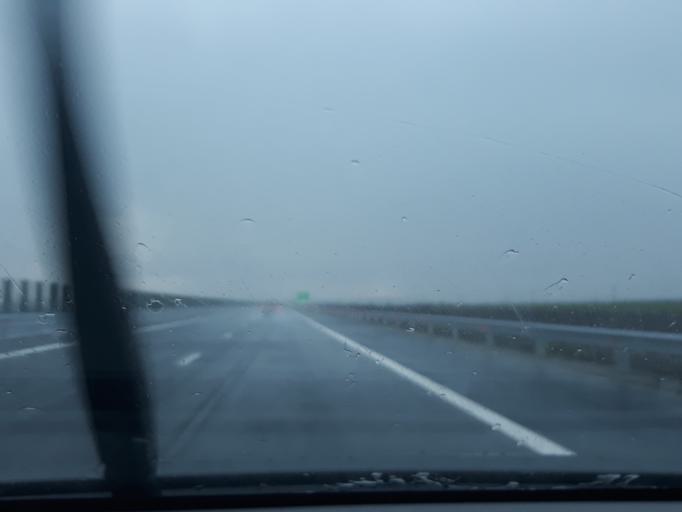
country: RO
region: Mures
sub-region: Comuna Ogra
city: Ogra
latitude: 46.4356
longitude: 24.3000
